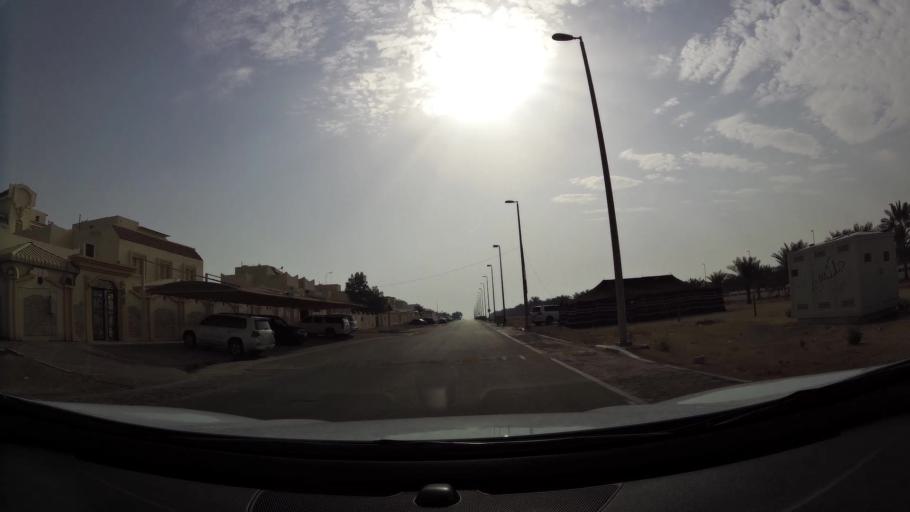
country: AE
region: Abu Dhabi
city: Abu Dhabi
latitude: 24.2387
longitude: 54.7207
